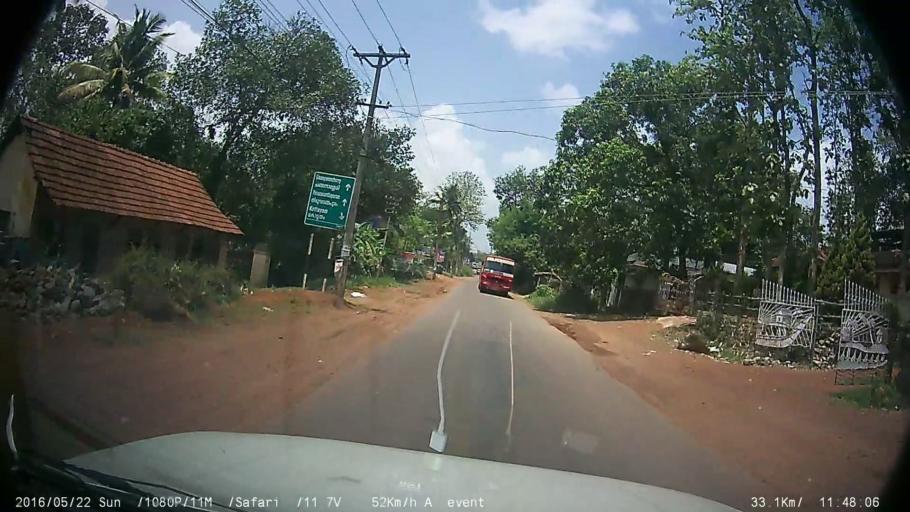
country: IN
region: Kerala
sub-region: Kottayam
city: Kottayam
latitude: 9.5266
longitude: 76.5245
